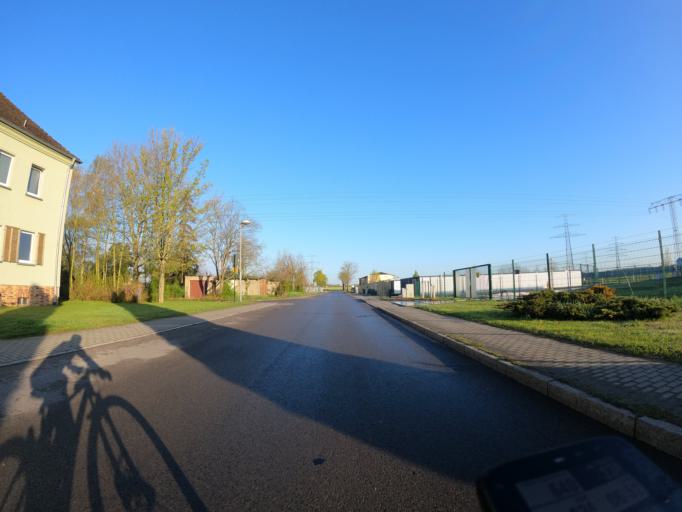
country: DE
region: Brandenburg
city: Neuenhagen
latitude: 52.5379
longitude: 13.7042
